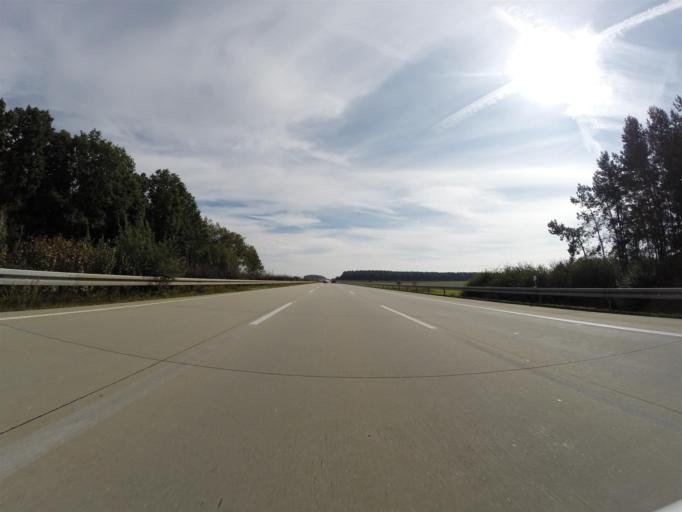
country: DE
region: Thuringia
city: Kraftsdorf
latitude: 50.8912
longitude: 11.9198
